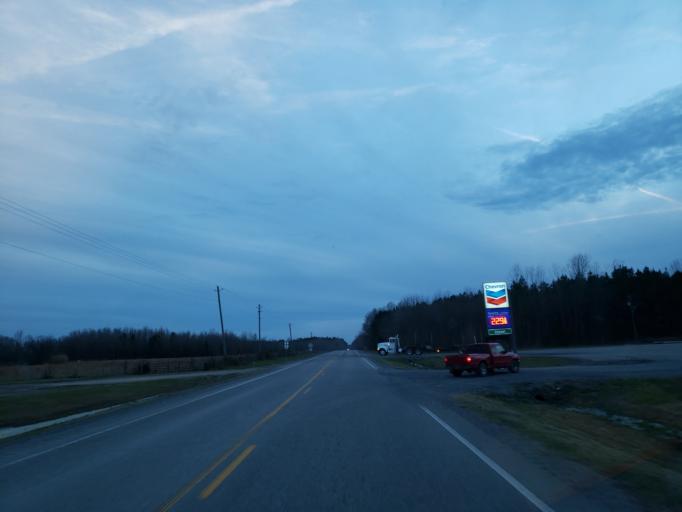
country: US
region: Alabama
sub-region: Sumter County
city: Livingston
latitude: 32.8311
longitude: -88.3093
